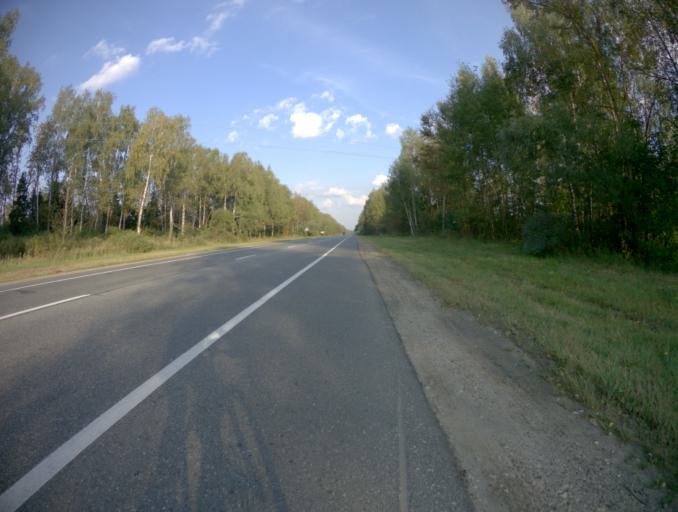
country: RU
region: Vladimir
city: Kameshkovo
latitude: 56.1978
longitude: 40.8521
